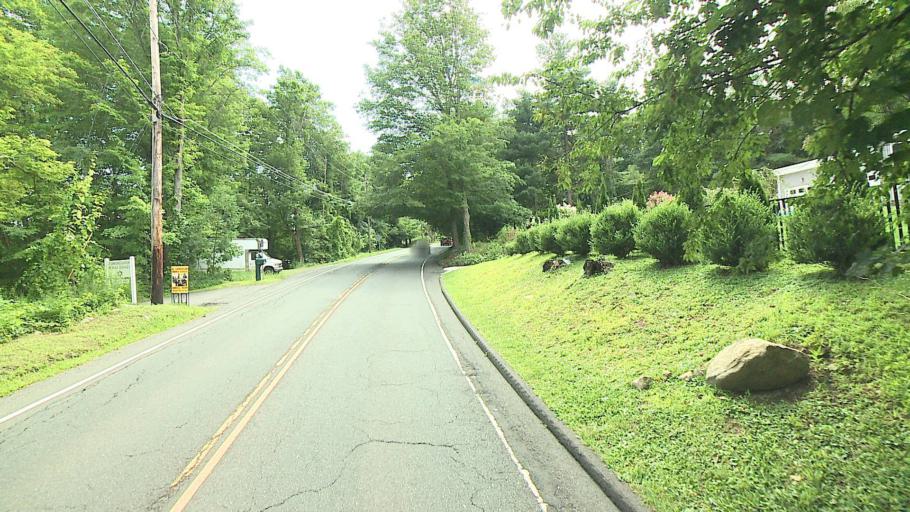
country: US
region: Connecticut
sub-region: Fairfield County
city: Danbury
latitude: 41.4347
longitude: -73.4951
